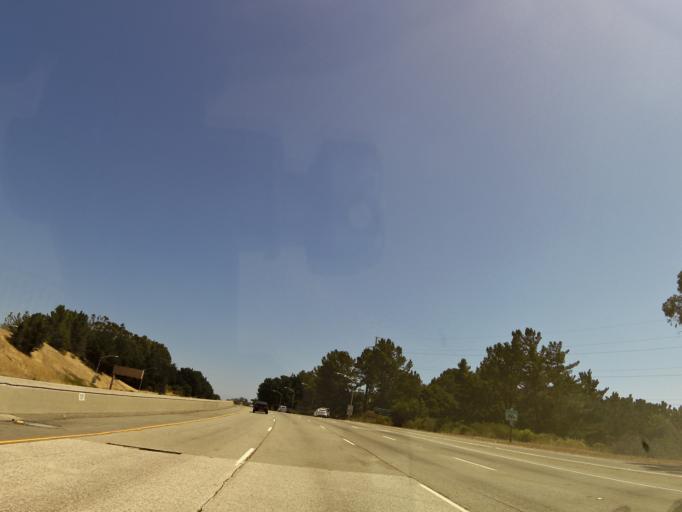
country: US
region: California
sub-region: San Mateo County
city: San Bruno
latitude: 37.6019
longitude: -122.4264
